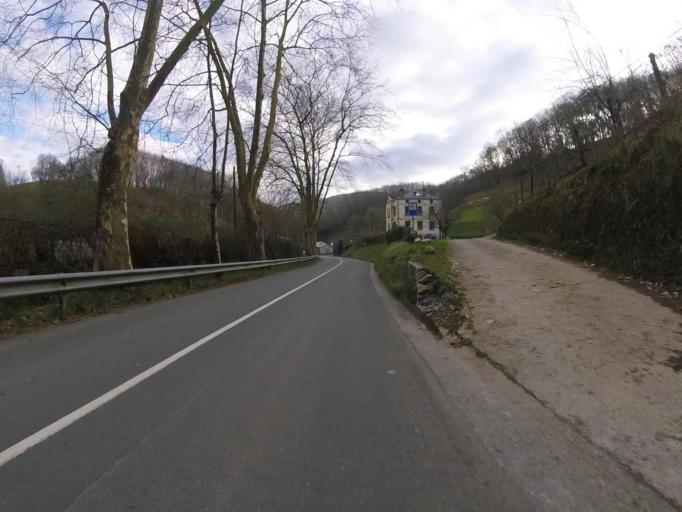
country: ES
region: Basque Country
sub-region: Provincia de Guipuzcoa
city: Irun
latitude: 43.3172
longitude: -1.8190
